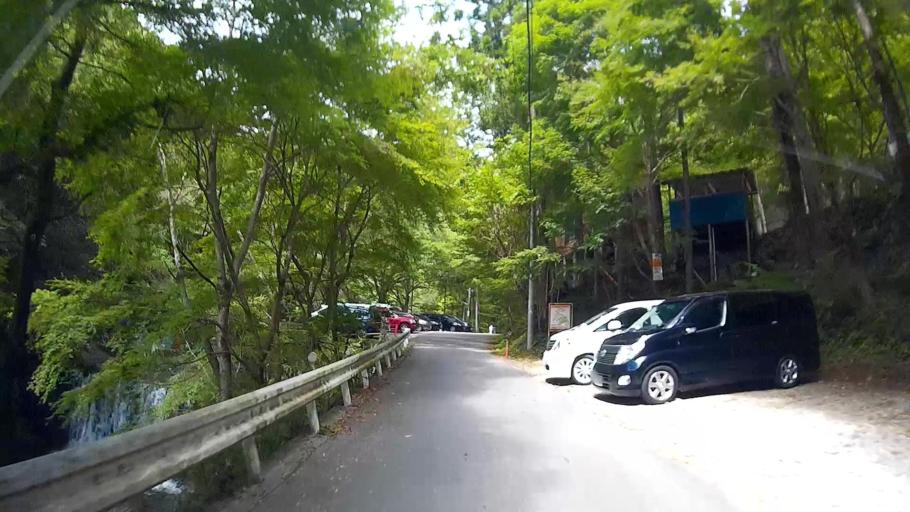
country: JP
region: Saitama
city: Chichibu
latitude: 35.9139
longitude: 139.1409
